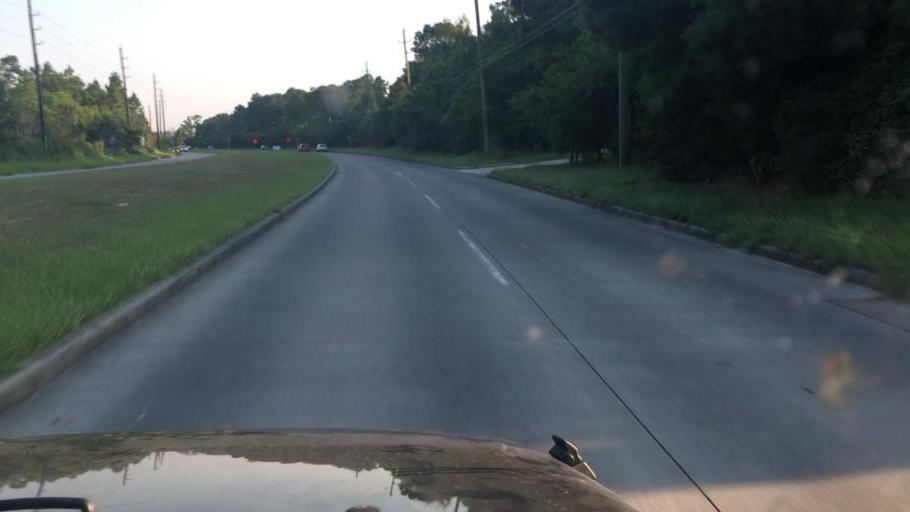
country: US
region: Texas
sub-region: Harris County
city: Atascocita
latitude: 29.9540
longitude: -95.1737
